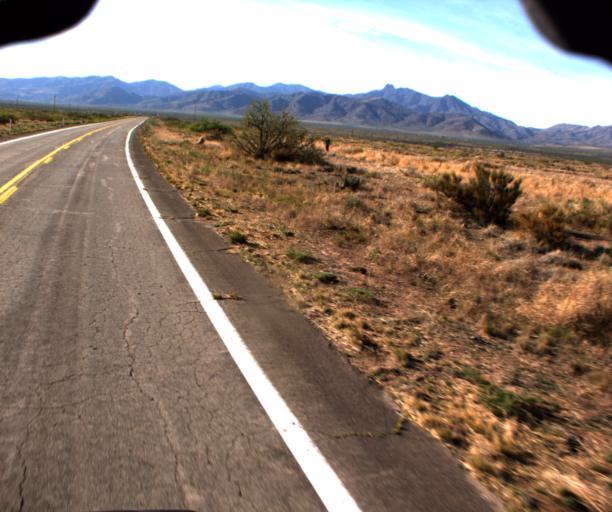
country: US
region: Arizona
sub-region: Cochise County
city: Willcox
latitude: 32.3686
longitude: -109.6245
